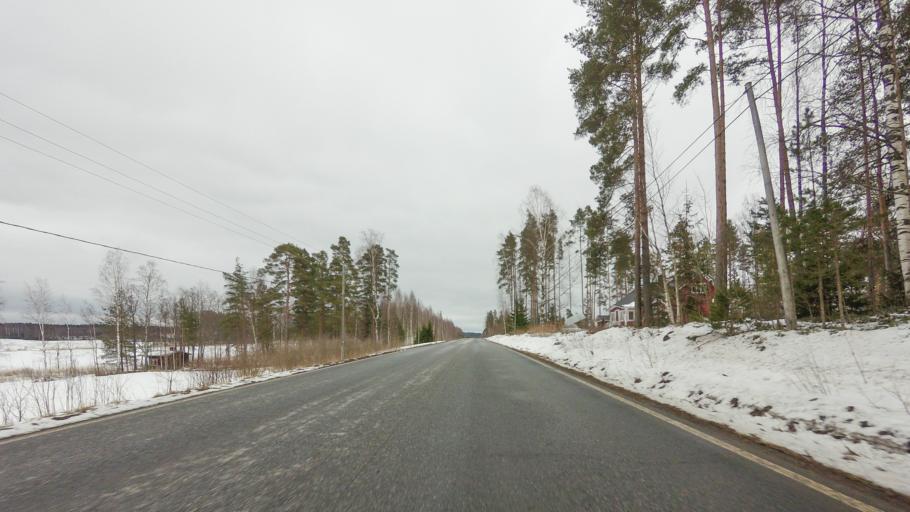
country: FI
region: Southern Savonia
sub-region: Savonlinna
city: Savonlinna
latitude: 61.9581
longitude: 28.8359
